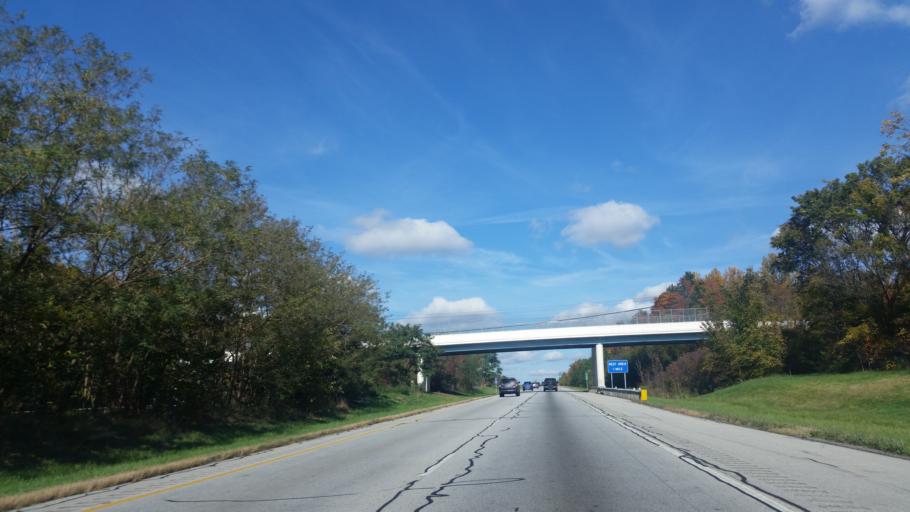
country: US
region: Ohio
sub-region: Summit County
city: Montrose-Ghent
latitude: 41.1744
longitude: -81.6257
